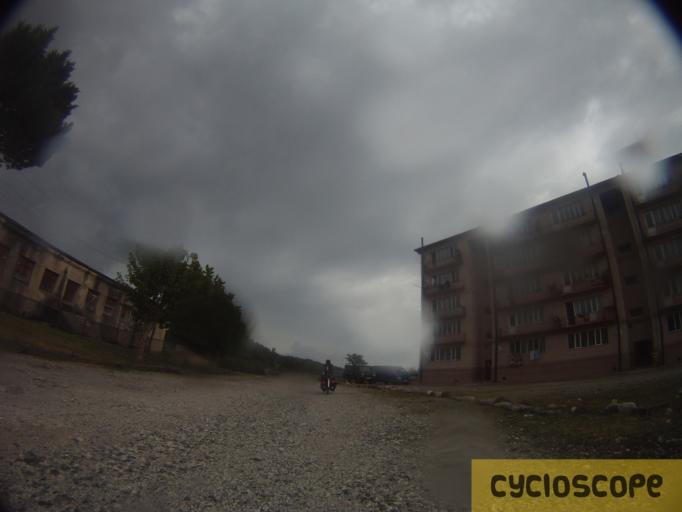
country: GE
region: Samegrelo and Zemo Svaneti
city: Jvari
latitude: 42.7882
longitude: 42.0532
